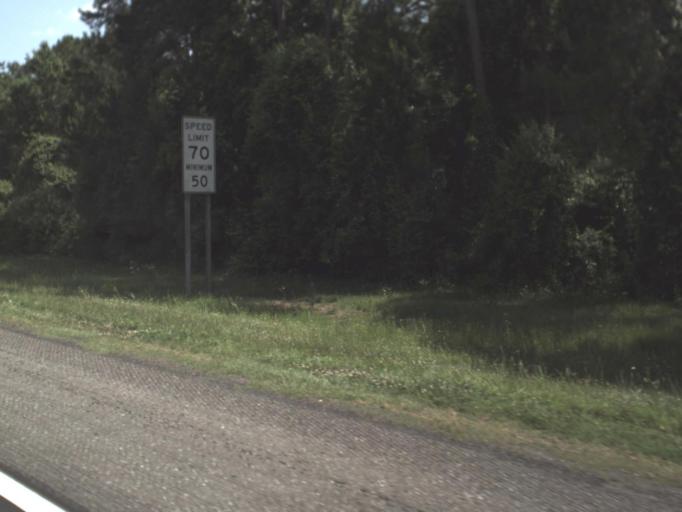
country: US
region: Florida
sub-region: Nassau County
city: Yulee
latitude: 30.5275
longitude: -81.6360
